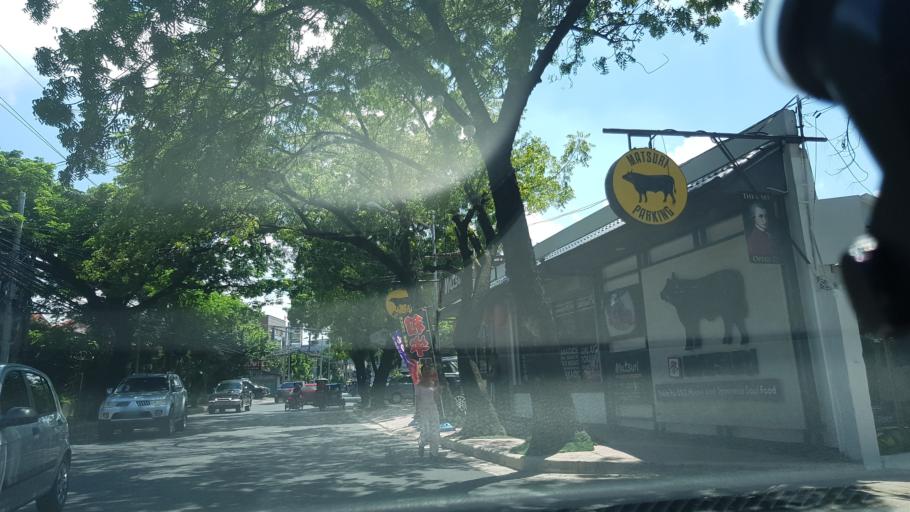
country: PH
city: Sambayanihan People's Village
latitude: 14.4515
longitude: 121.0301
